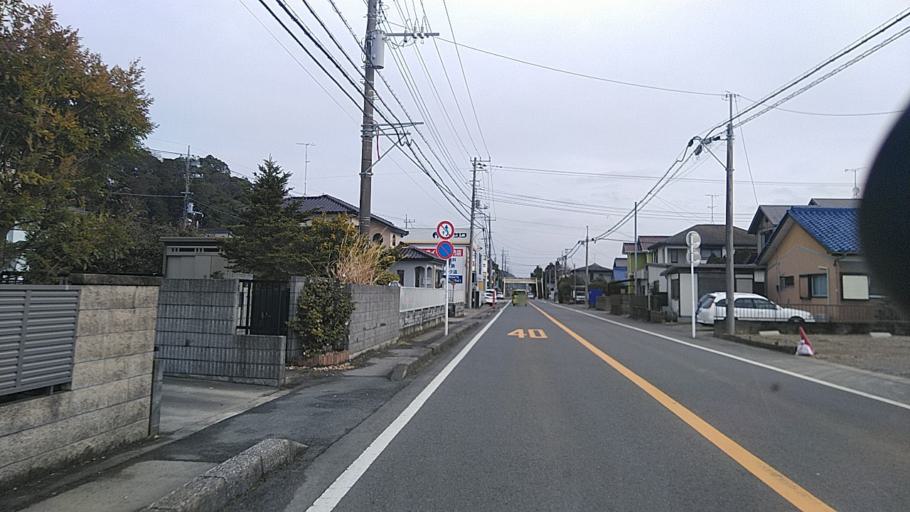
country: JP
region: Chiba
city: Togane
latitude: 35.5832
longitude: 140.3804
